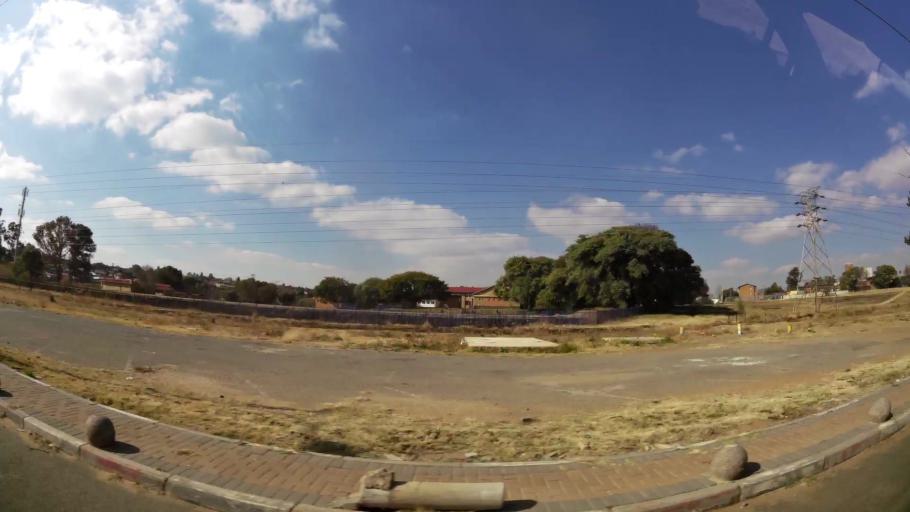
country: ZA
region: Gauteng
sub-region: West Rand District Municipality
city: Krugersdorp
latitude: -26.0977
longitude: 27.7632
